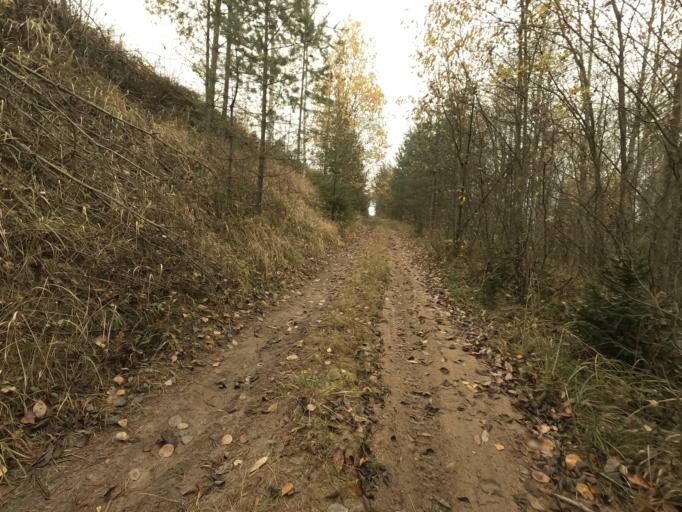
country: RU
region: Leningrad
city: Pavlovo
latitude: 59.7730
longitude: 30.9039
